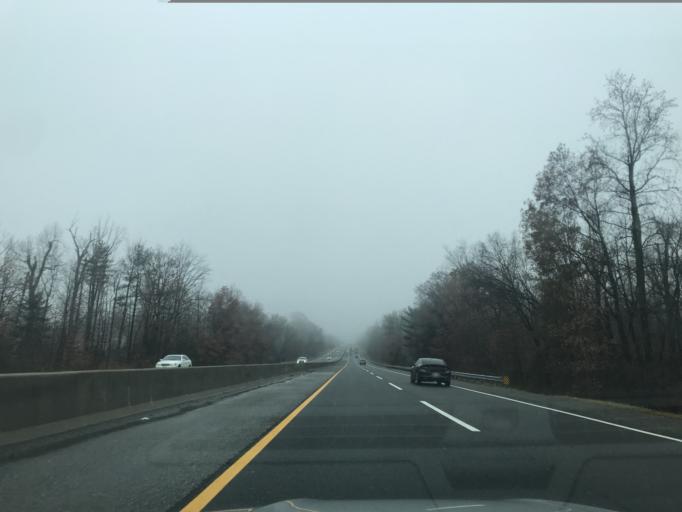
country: US
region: New Jersey
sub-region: Gloucester County
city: Oak Valley
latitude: 39.7957
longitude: -75.2035
